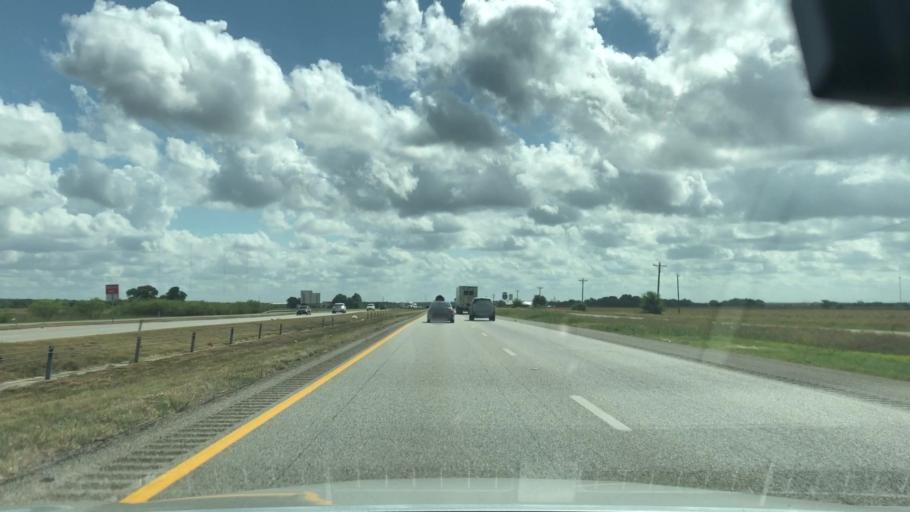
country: US
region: Texas
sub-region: Guadalupe County
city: Marion
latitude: 29.5211
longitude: -98.1340
